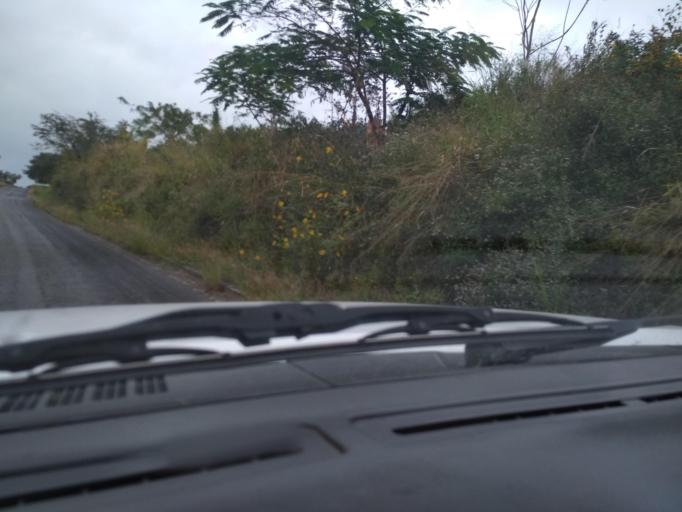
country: MX
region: Veracruz
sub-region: Emiliano Zapata
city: Dos Rios
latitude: 19.5287
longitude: -96.7978
